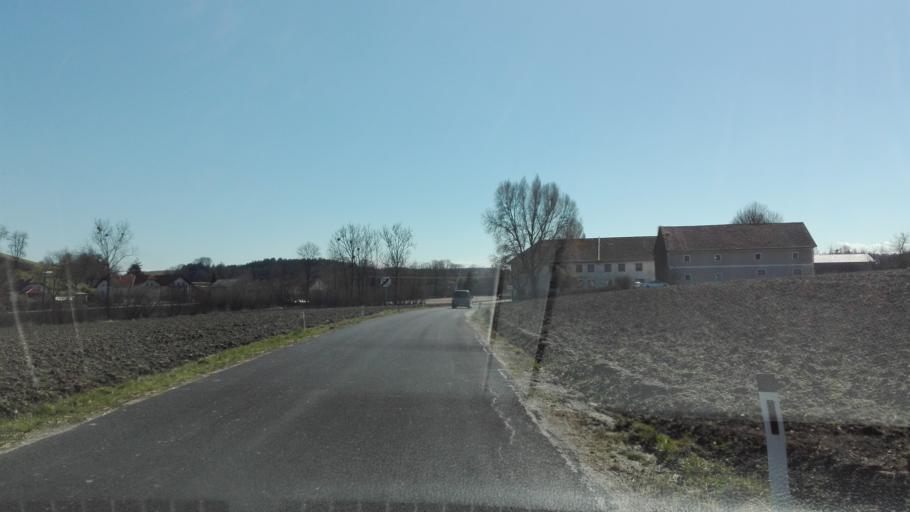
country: AT
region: Upper Austria
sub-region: Wels-Land
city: Buchkirchen
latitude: 48.2184
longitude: 13.9711
